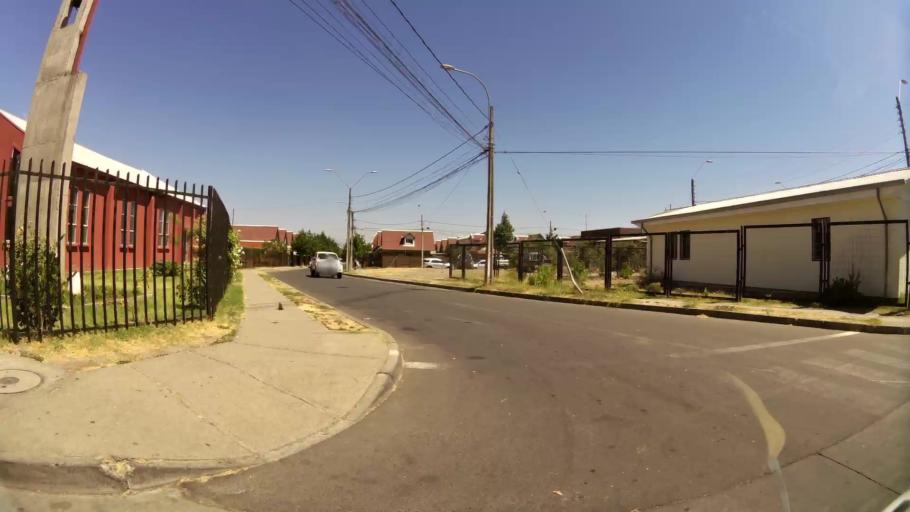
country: CL
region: Maule
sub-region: Provincia de Curico
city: Curico
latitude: -34.9694
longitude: -71.2221
